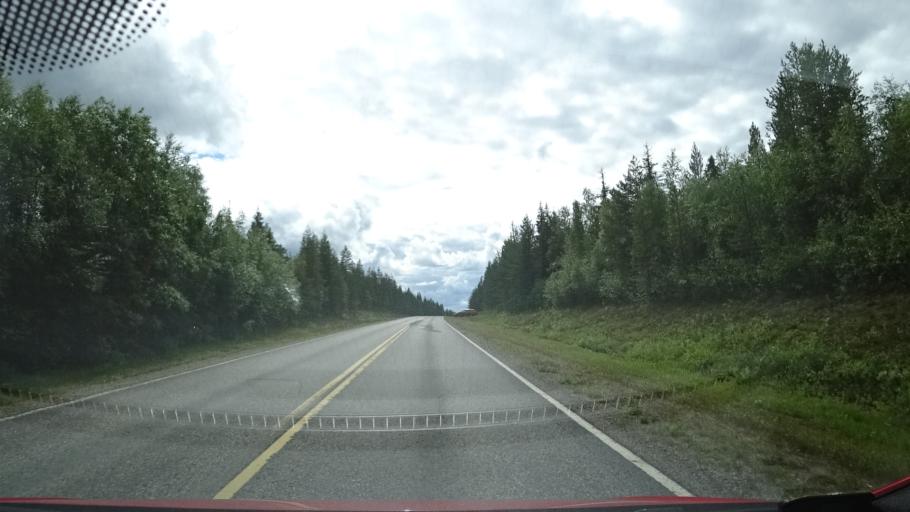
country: FI
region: Lapland
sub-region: Tunturi-Lappi
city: Kittilae
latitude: 67.5559
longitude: 24.9224
